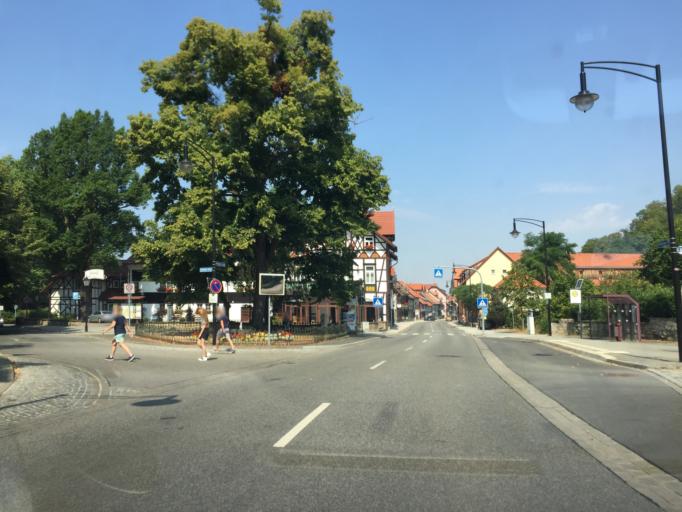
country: DE
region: Saxony-Anhalt
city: Wernigerode
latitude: 51.8276
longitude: 10.7943
